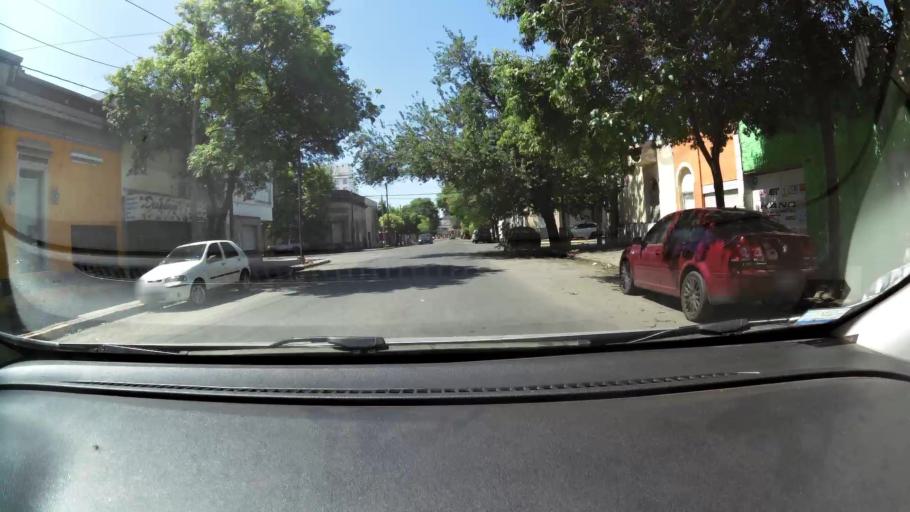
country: AR
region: Cordoba
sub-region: Departamento de Capital
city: Cordoba
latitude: -31.3904
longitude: -64.1880
